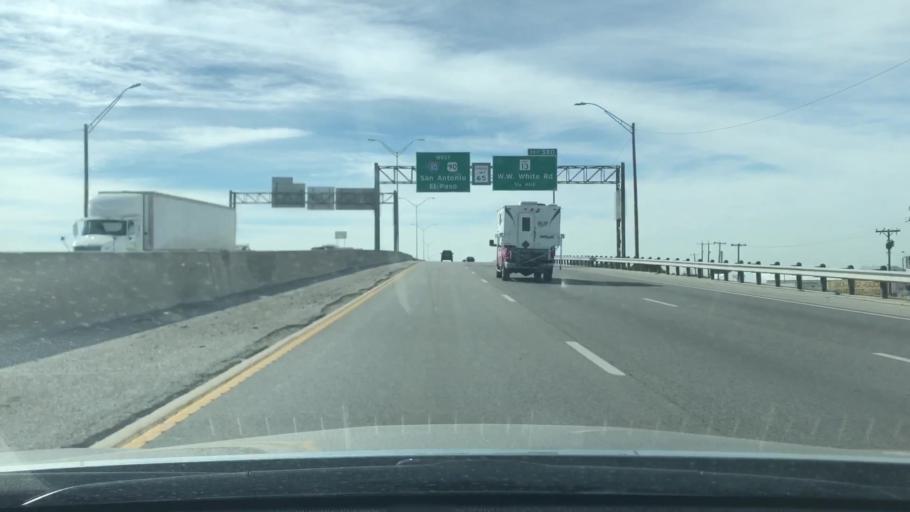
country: US
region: Texas
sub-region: Bexar County
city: Kirby
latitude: 29.4336
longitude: -98.3979
